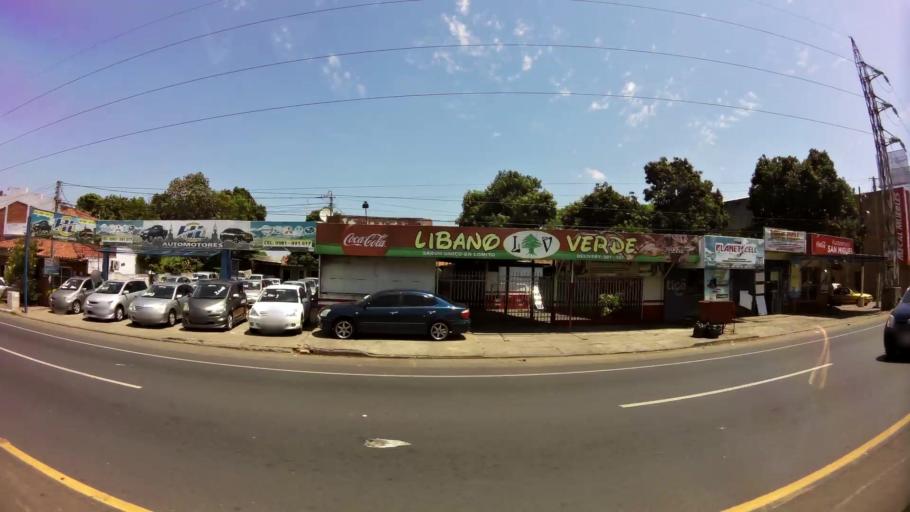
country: PY
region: Central
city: Villa Elisa
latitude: -25.3502
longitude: -57.5730
